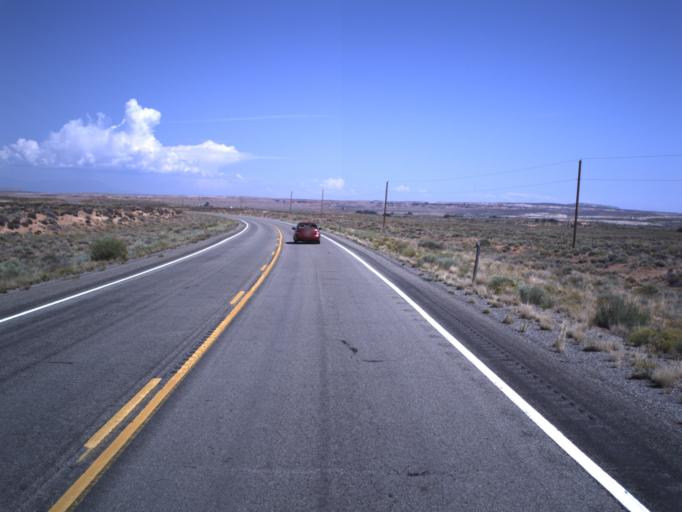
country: US
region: Utah
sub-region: San Juan County
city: Blanding
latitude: 37.0746
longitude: -109.5492
